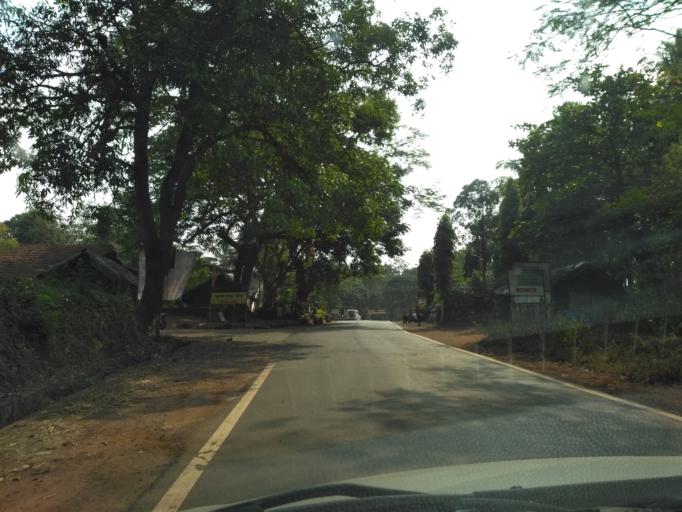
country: IN
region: Goa
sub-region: North Goa
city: Pernem
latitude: 15.7603
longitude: 73.9249
